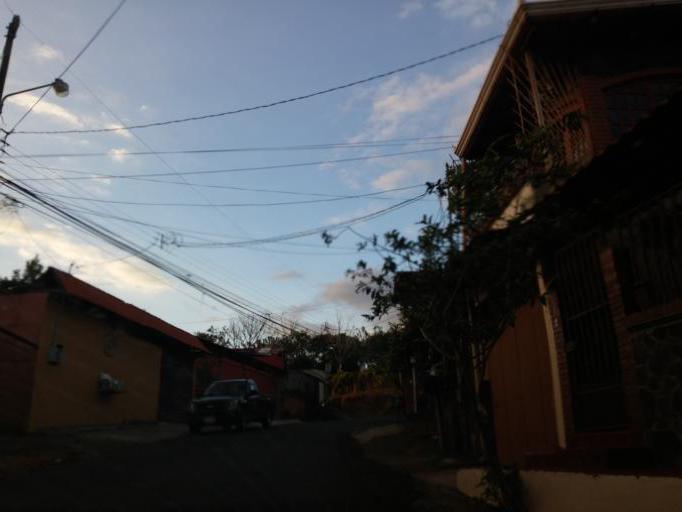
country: CR
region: Alajuela
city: Alajuela
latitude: 10.0385
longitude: -84.2077
